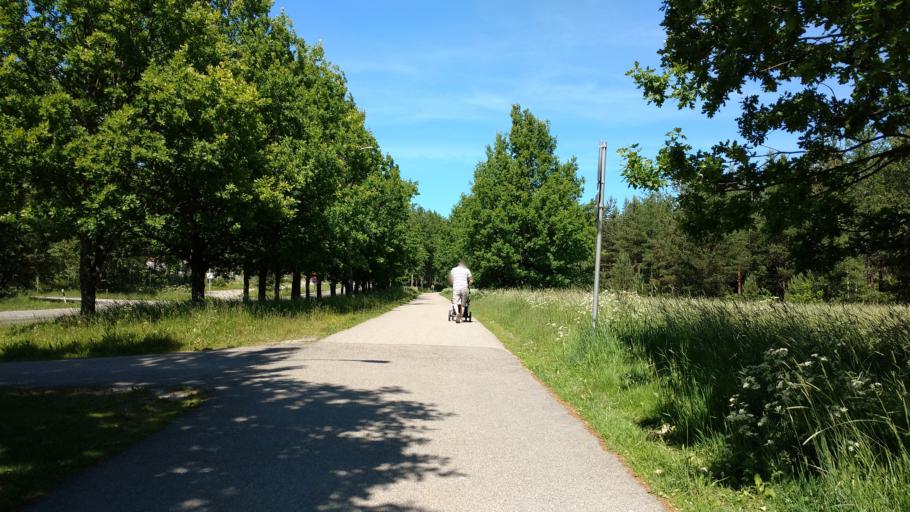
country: FI
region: Varsinais-Suomi
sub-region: Salo
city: Salo
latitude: 60.3962
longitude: 23.1256
